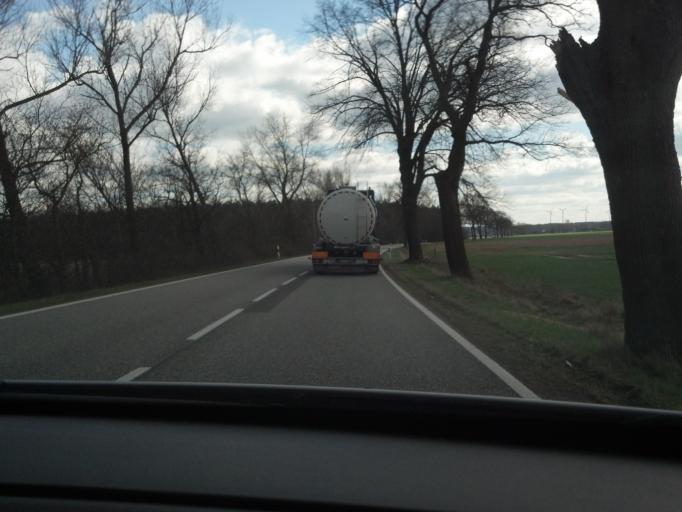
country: DE
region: Brandenburg
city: Gerdshagen
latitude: 53.3356
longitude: 12.2463
